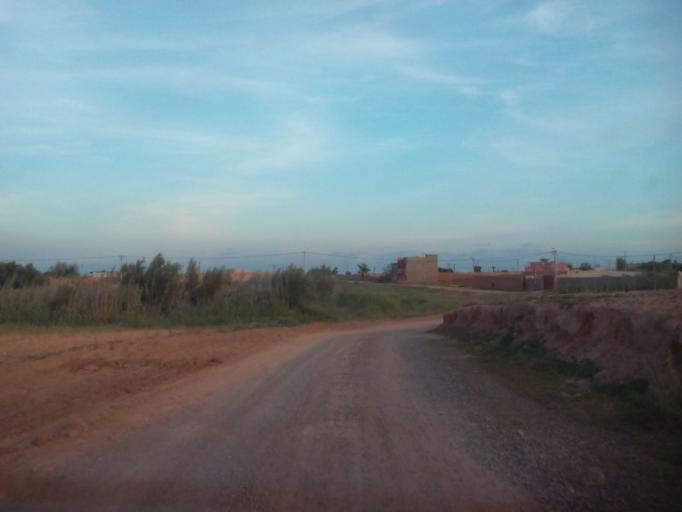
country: MA
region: Marrakech-Tensift-Al Haouz
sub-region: Marrakech
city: Marrakesh
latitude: 31.6288
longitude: -8.2881
